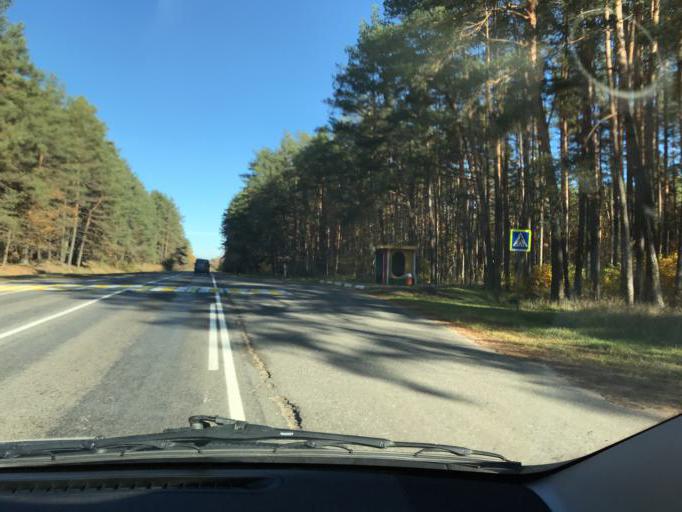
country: BY
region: Vitebsk
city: Polatsk
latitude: 55.3192
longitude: 28.7789
